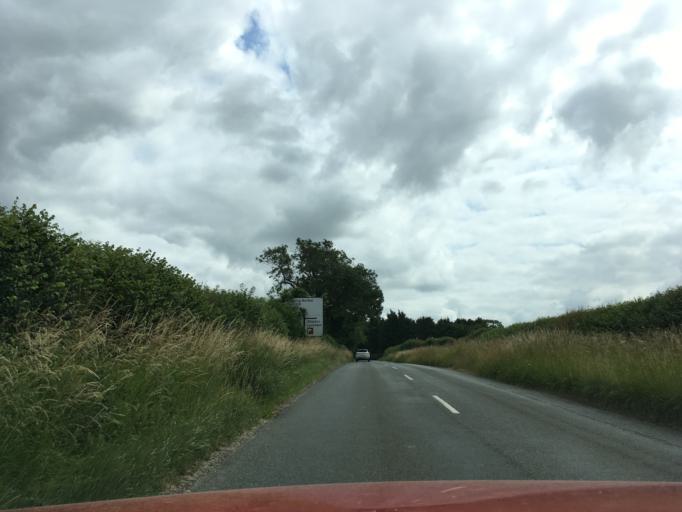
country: GB
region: England
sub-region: Oxfordshire
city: Shipton under Wychwood
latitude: 51.9017
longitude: -1.6121
